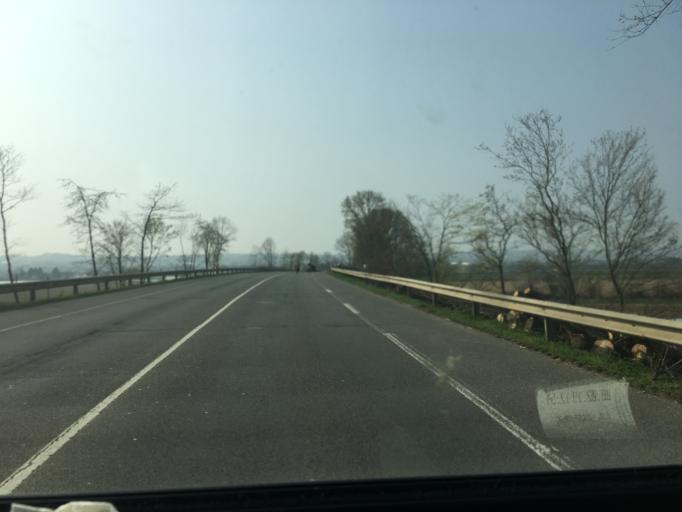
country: DE
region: North Rhine-Westphalia
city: Bornheim
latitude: 50.7763
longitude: 6.9883
